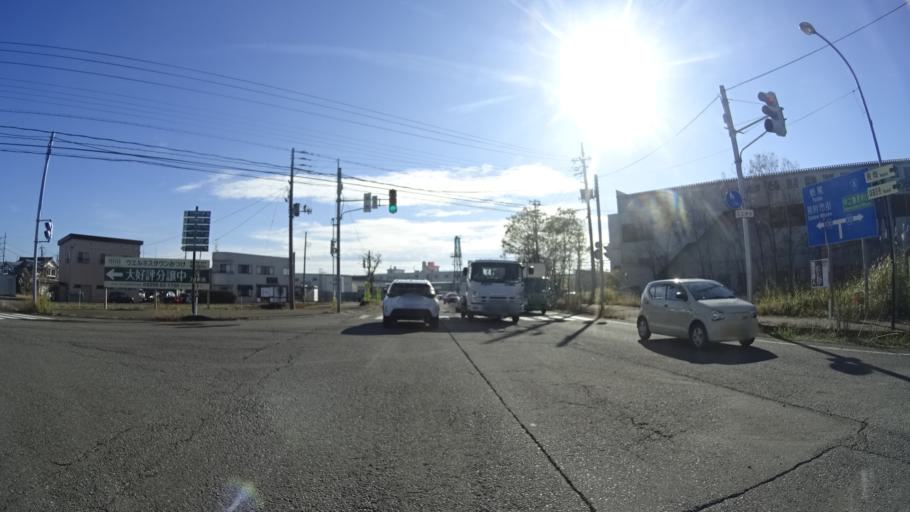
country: JP
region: Niigata
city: Mitsuke
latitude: 37.5409
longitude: 138.8996
